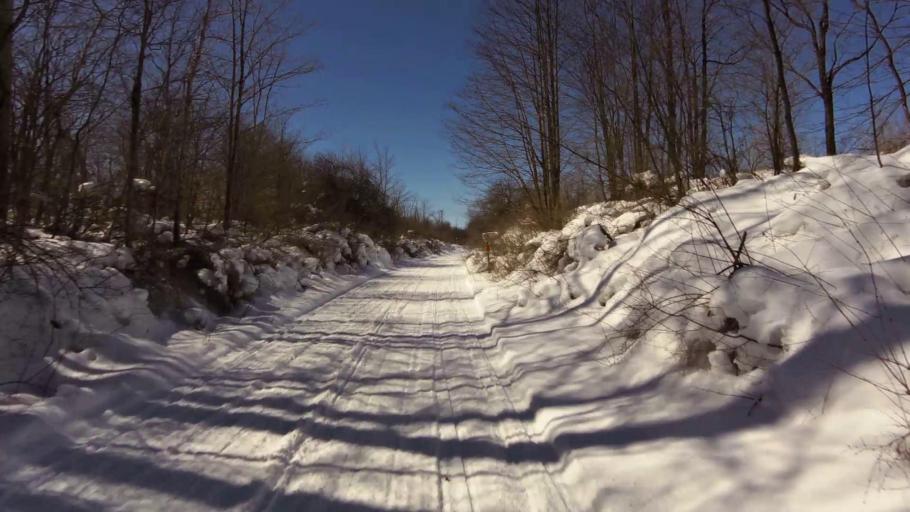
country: US
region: New York
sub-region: Cattaraugus County
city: Franklinville
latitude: 42.4227
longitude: -78.3720
